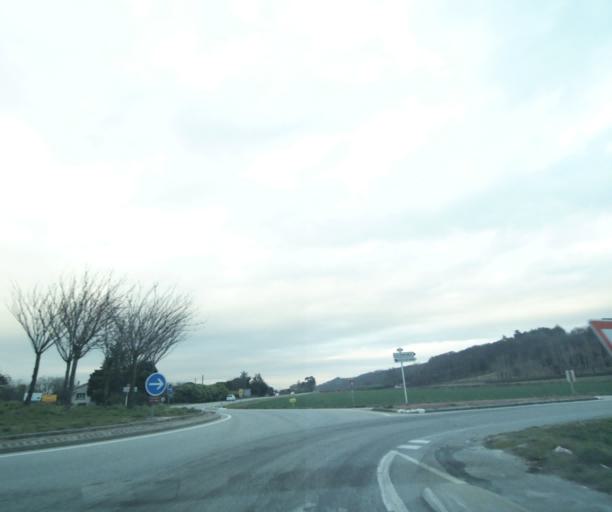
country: FR
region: Rhone-Alpes
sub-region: Departement de la Drome
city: Bourg-les-Valence
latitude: 44.9828
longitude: 4.8998
